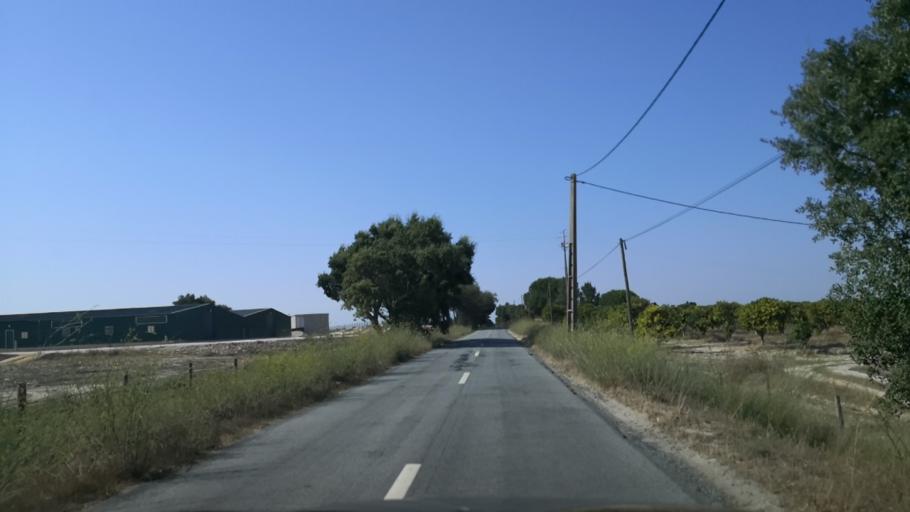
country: PT
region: Evora
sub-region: Vendas Novas
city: Vendas Novas
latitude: 38.7198
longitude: -8.6190
